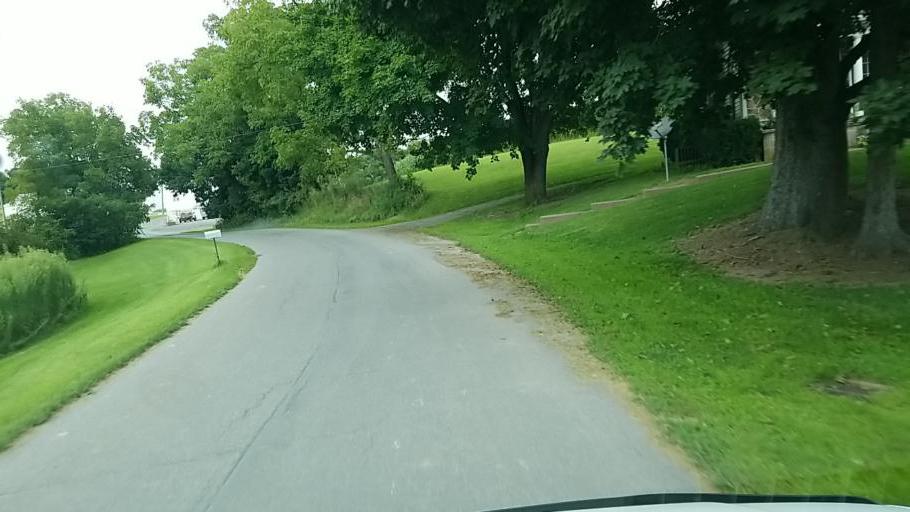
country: US
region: Pennsylvania
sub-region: Dauphin County
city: Elizabethville
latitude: 40.5999
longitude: -76.8038
